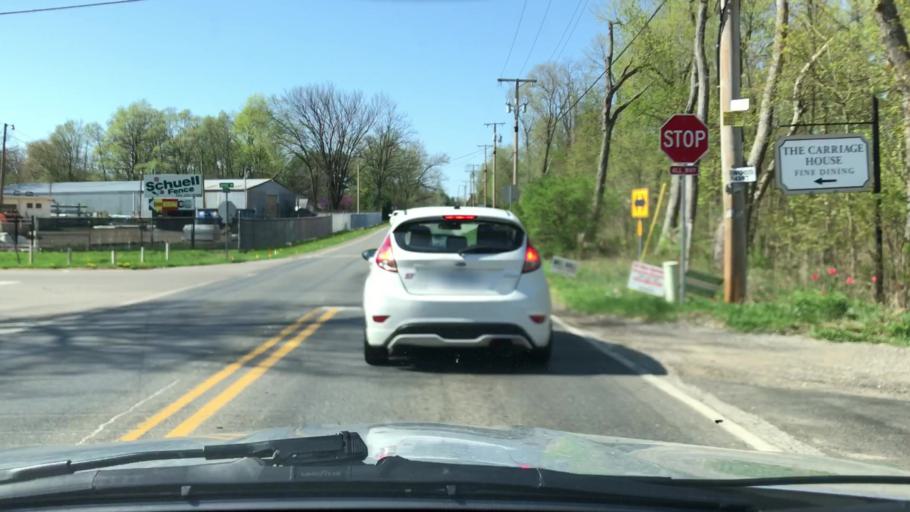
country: US
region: Indiana
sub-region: Saint Joseph County
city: Georgetown
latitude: 41.7518
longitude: -86.3008
